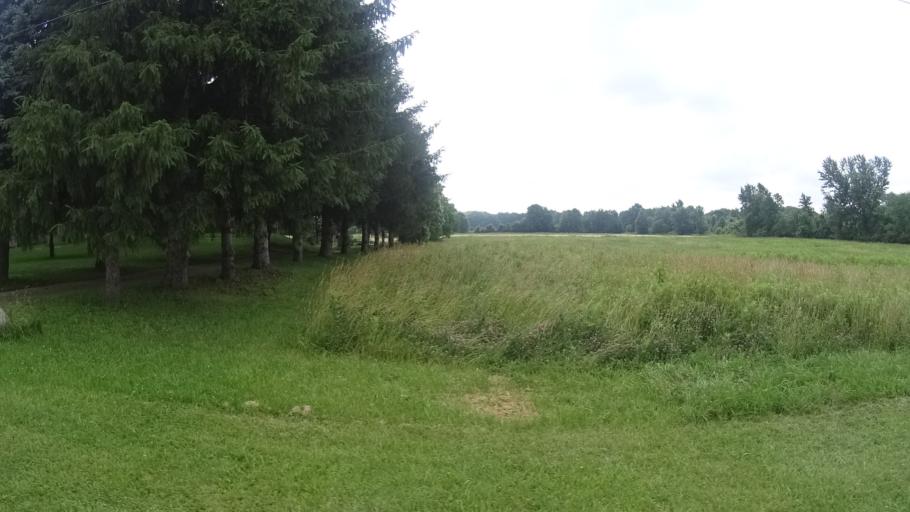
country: US
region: Ohio
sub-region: Huron County
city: Wakeman
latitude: 41.3289
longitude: -82.4386
